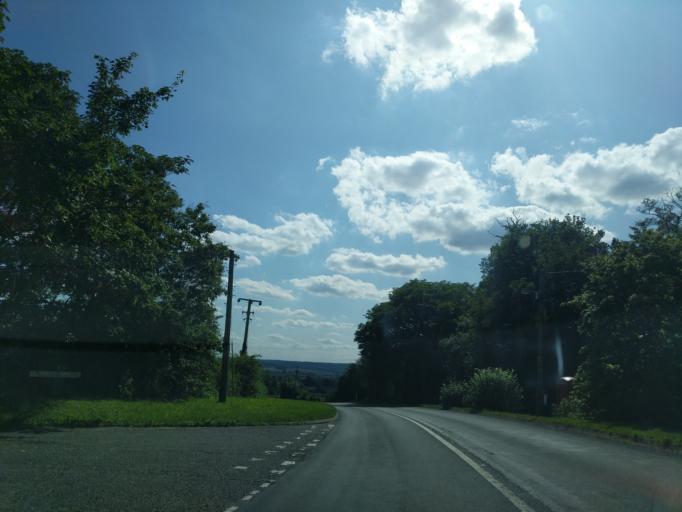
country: GB
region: England
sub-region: Staffordshire
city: Rugeley
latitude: 52.8063
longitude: -1.9265
